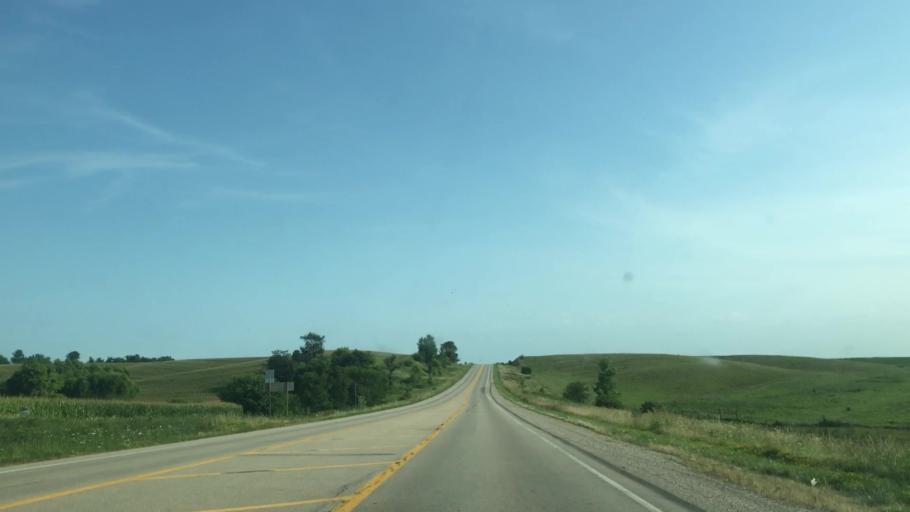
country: US
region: Iowa
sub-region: Marshall County
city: Marshalltown
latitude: 42.0479
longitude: -93.0003
